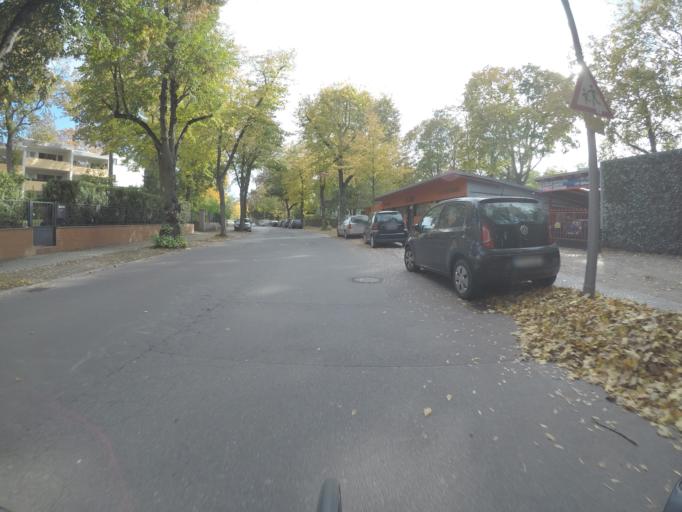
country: DE
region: Berlin
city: Hermsdorf
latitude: 52.6195
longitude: 13.3067
